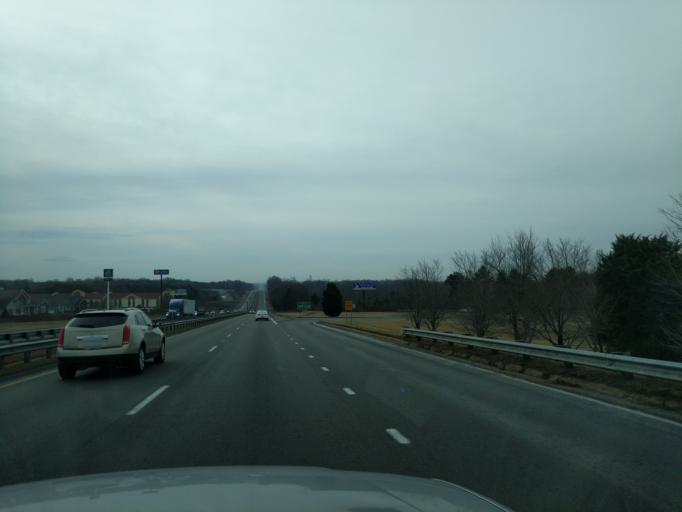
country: US
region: North Carolina
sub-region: Iredell County
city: Statesville
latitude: 35.7723
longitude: -80.8632
